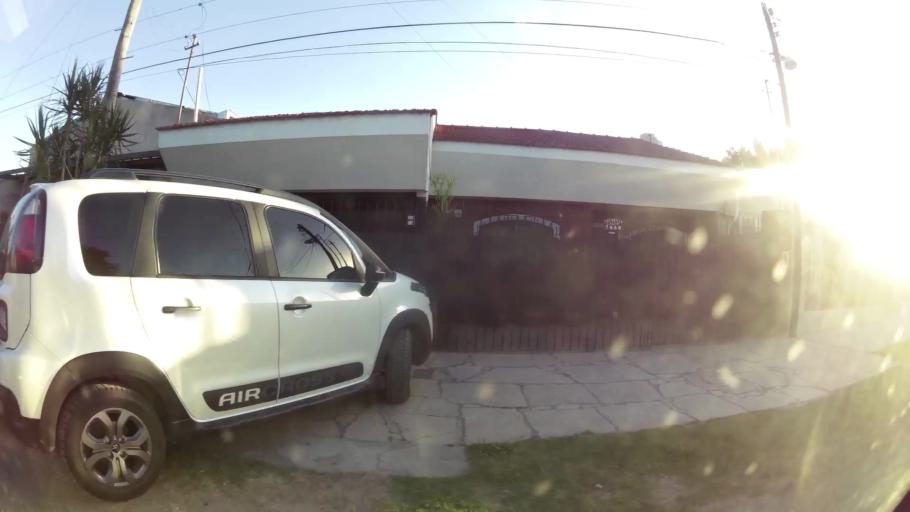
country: AR
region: Santa Fe
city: Santa Fe de la Vera Cruz
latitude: -31.5991
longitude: -60.6861
